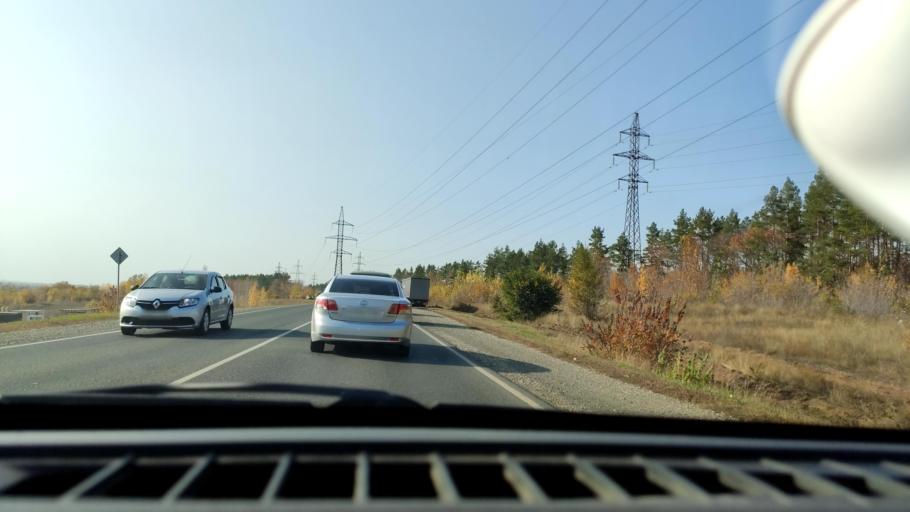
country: RU
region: Samara
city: Samara
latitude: 53.1236
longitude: 50.2068
